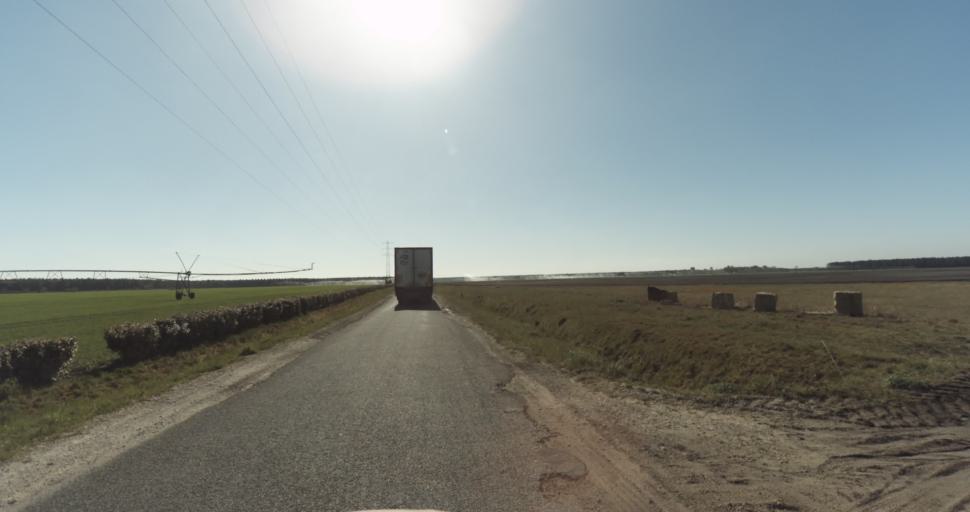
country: FR
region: Aquitaine
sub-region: Departement de la Gironde
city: Marcheprime
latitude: 44.7482
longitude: -0.8418
